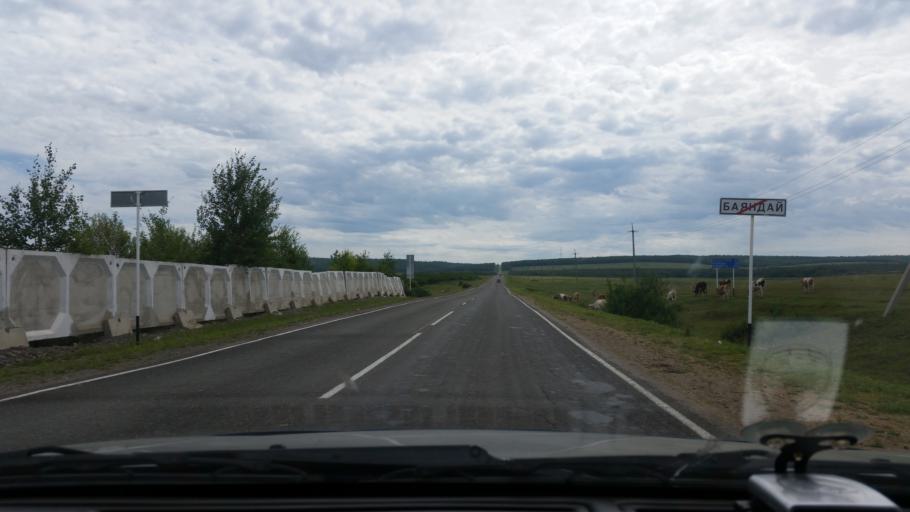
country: RU
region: Irkutsk
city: Bayanday
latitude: 53.0522
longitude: 105.5278
